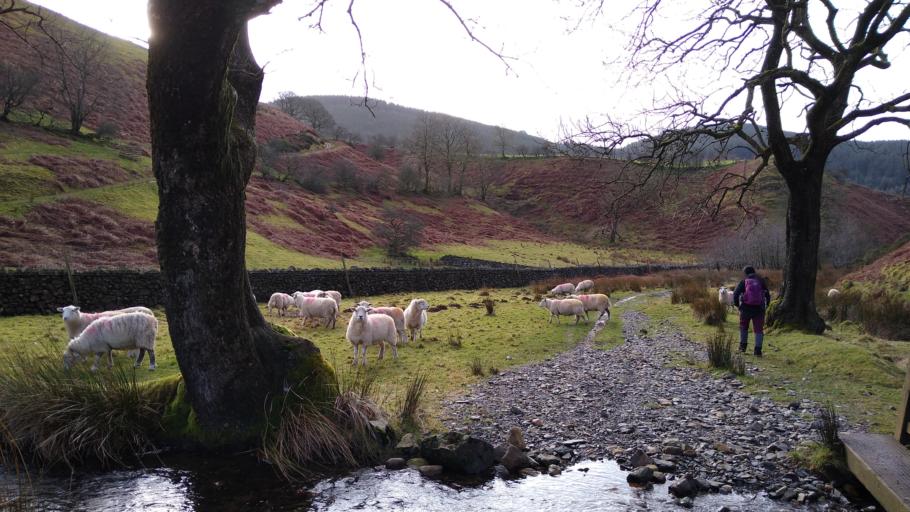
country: GB
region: England
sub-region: Cumbria
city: Frizington
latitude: 54.5027
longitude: -3.4600
